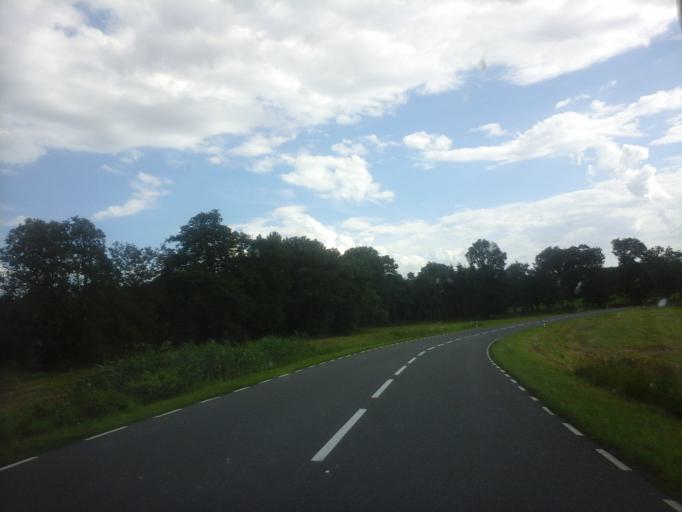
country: PL
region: West Pomeranian Voivodeship
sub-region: Powiat stargardzki
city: Suchan
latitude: 53.2524
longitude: 15.3331
